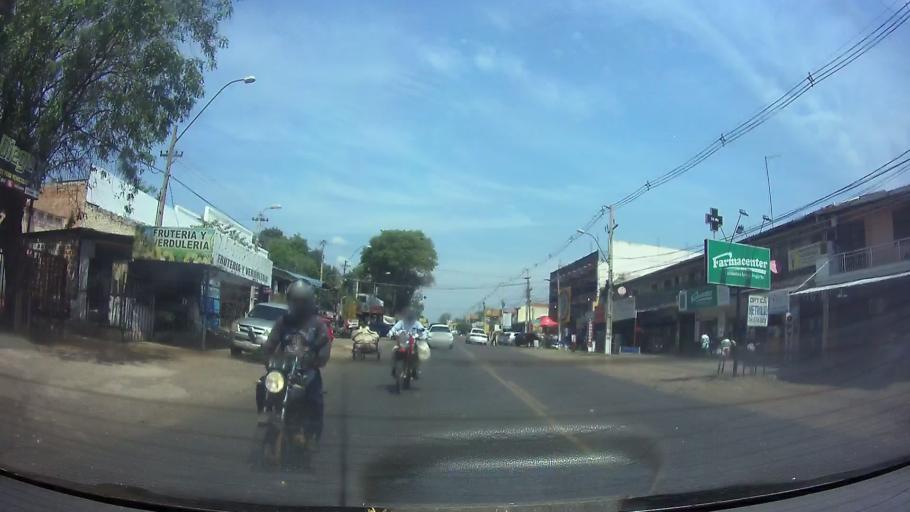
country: PY
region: Central
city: Capiata
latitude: -25.3666
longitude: -57.4815
